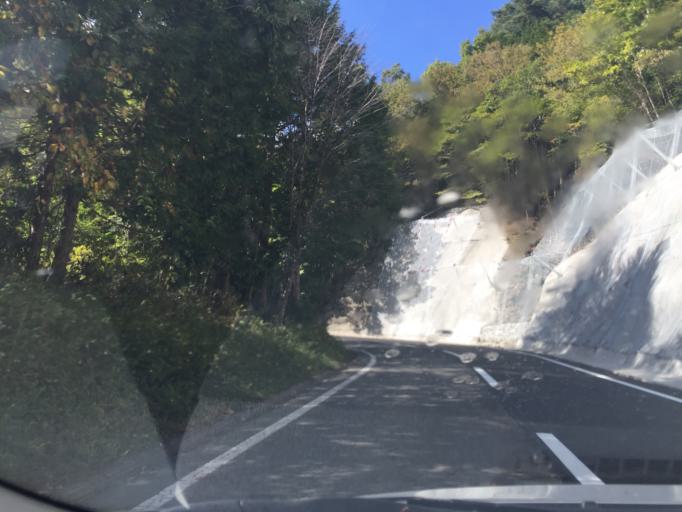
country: JP
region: Gifu
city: Nakatsugawa
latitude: 35.2989
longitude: 137.6739
